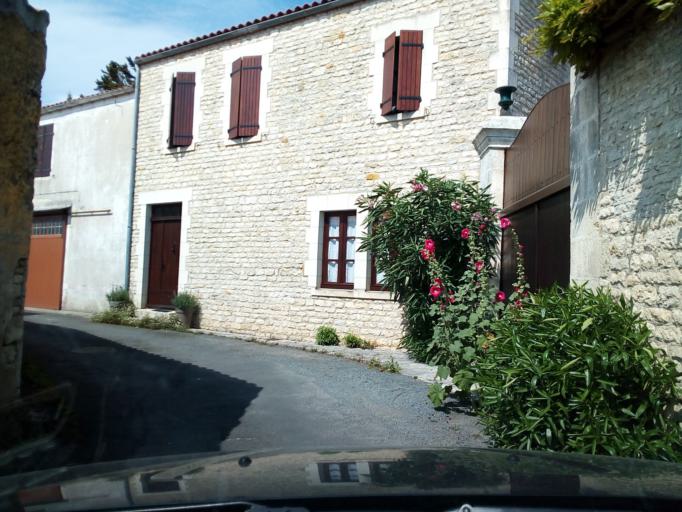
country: FR
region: Poitou-Charentes
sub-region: Departement de la Charente-Maritime
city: Dolus-d'Oleron
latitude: 45.9441
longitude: -1.3031
